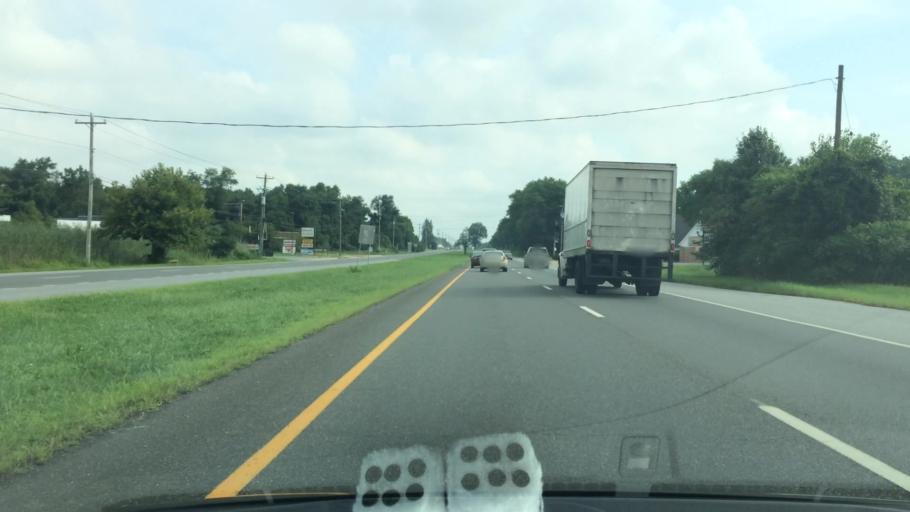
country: US
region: Delaware
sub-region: New Castle County
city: Bear
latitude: 39.6211
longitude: -75.6414
